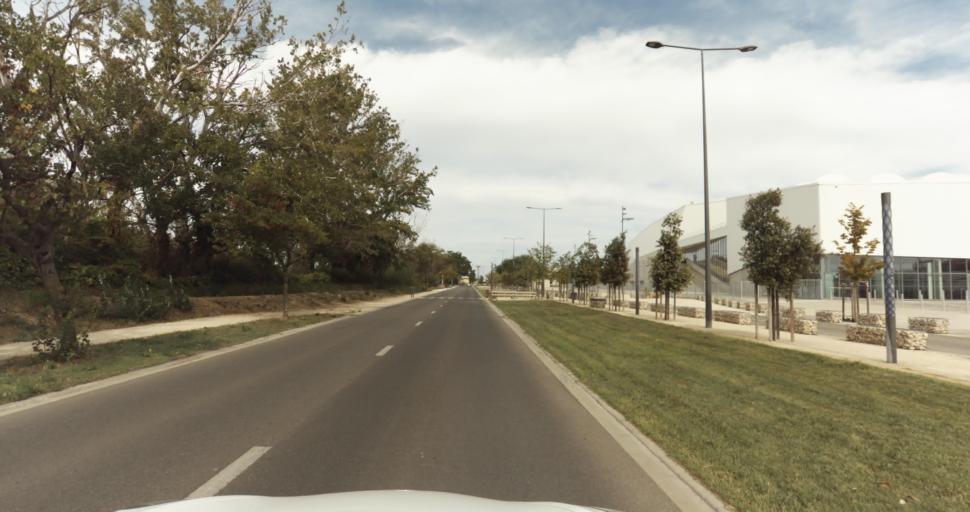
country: FR
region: Provence-Alpes-Cote d'Azur
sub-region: Departement des Bouches-du-Rhone
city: Miramas
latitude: 43.5929
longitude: 4.9996
